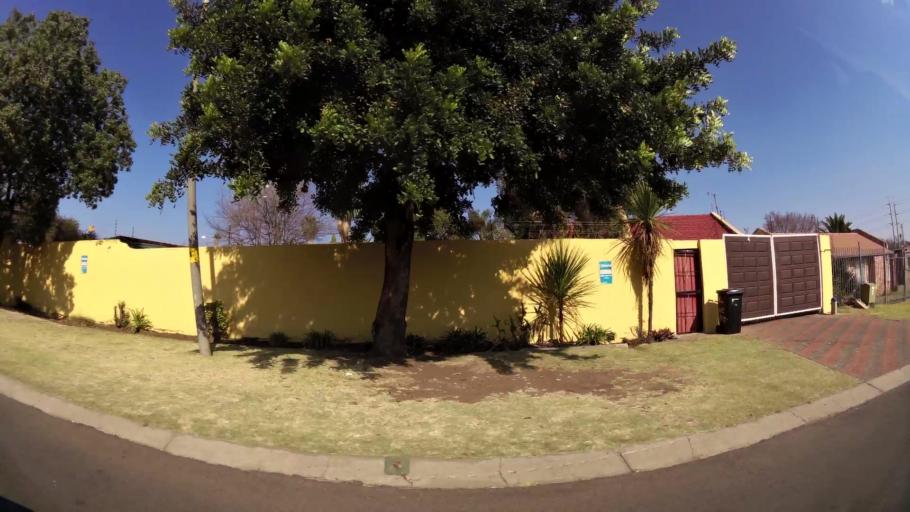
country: ZA
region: Gauteng
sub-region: City of Johannesburg Metropolitan Municipality
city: Modderfontein
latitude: -26.1201
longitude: 28.2231
